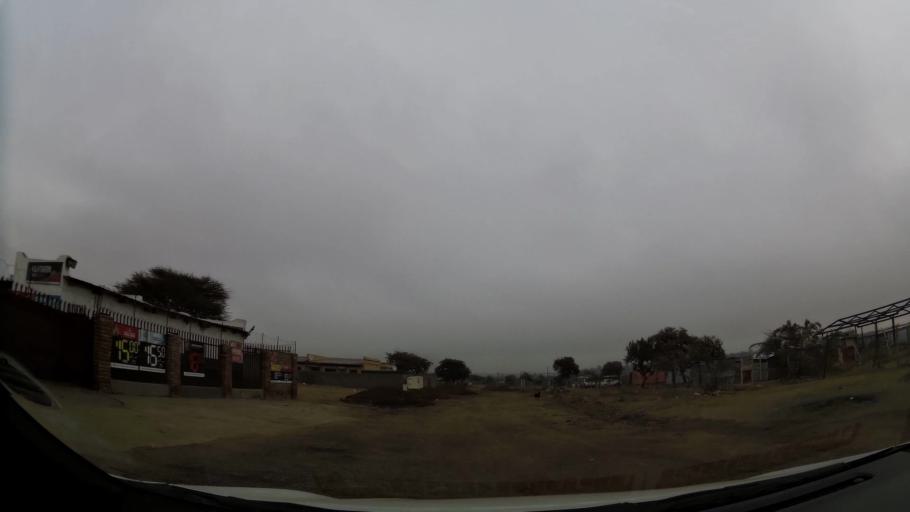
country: ZA
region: Limpopo
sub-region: Capricorn District Municipality
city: Polokwane
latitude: -23.8327
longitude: 29.3880
